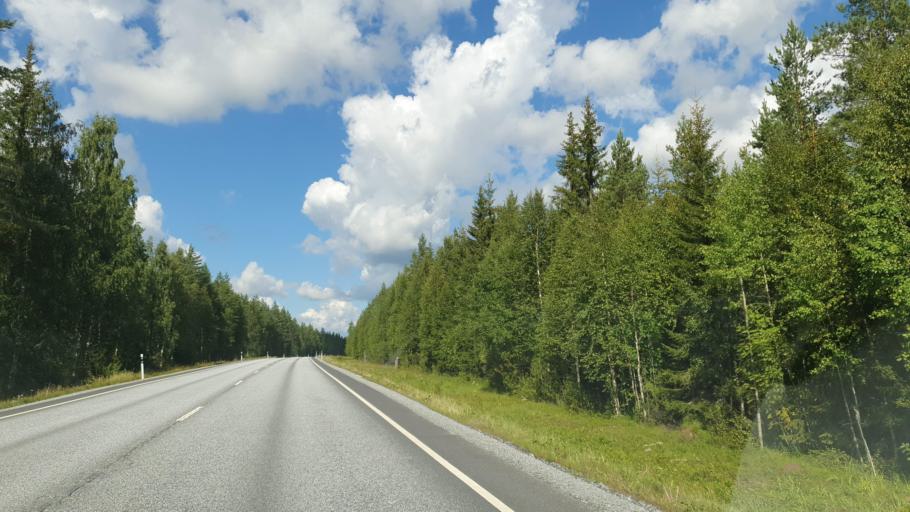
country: FI
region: Northern Savo
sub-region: Ylae-Savo
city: Sonkajaervi
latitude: 63.9012
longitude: 27.3962
